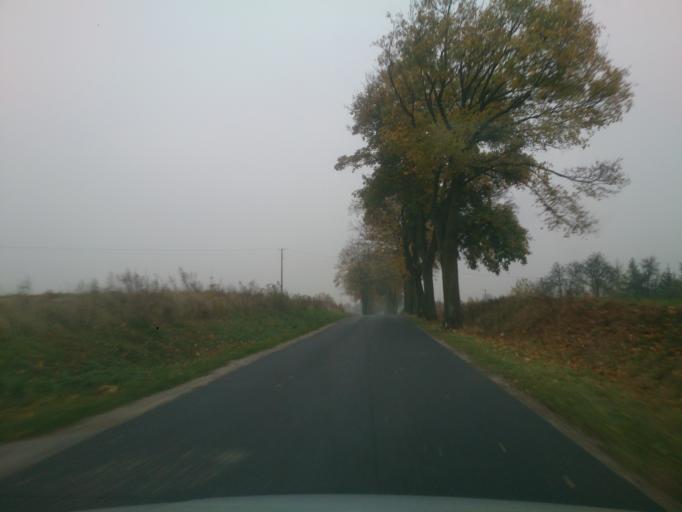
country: PL
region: Kujawsko-Pomorskie
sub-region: Powiat brodnicki
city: Brodnica
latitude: 53.3094
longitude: 19.3914
